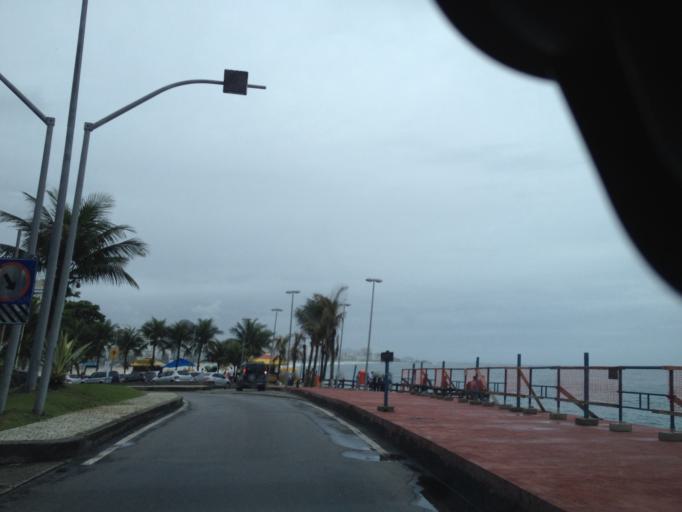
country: BR
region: Rio de Janeiro
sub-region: Rio De Janeiro
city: Rio de Janeiro
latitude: -22.9902
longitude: -43.2281
